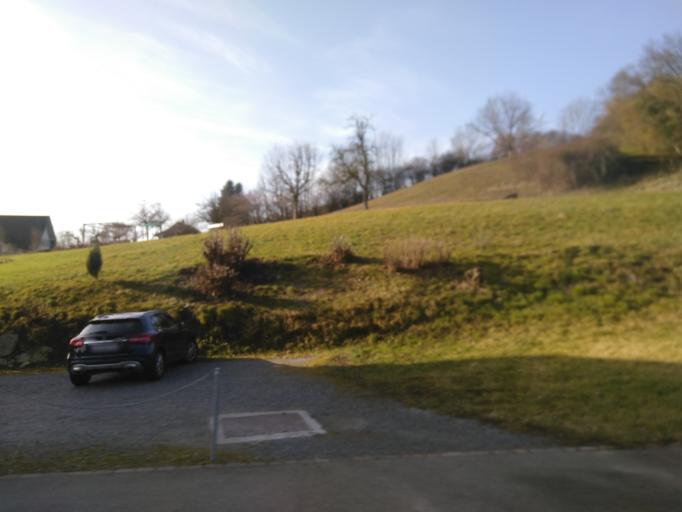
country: CH
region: Zurich
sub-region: Bezirk Hinwil
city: Gruet
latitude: 47.2946
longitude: 8.7782
